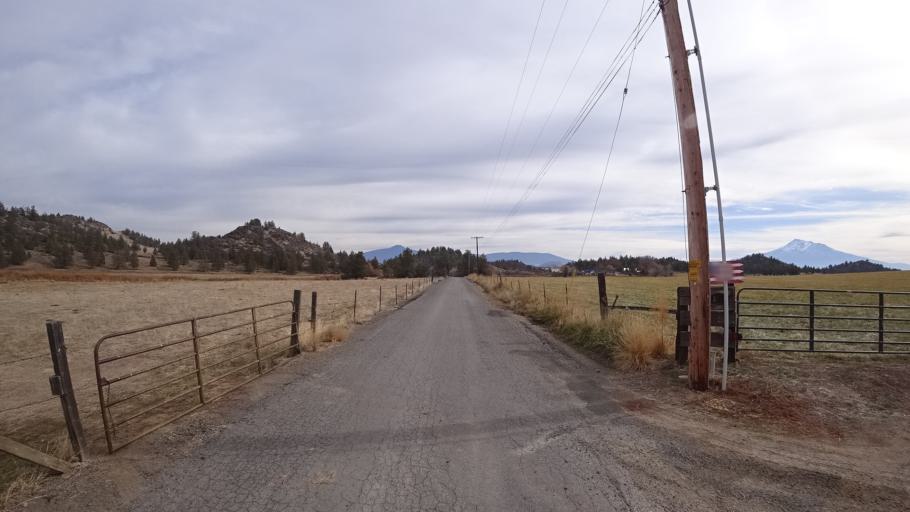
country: US
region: California
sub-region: Siskiyou County
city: Montague
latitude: 41.6833
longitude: -122.5201
